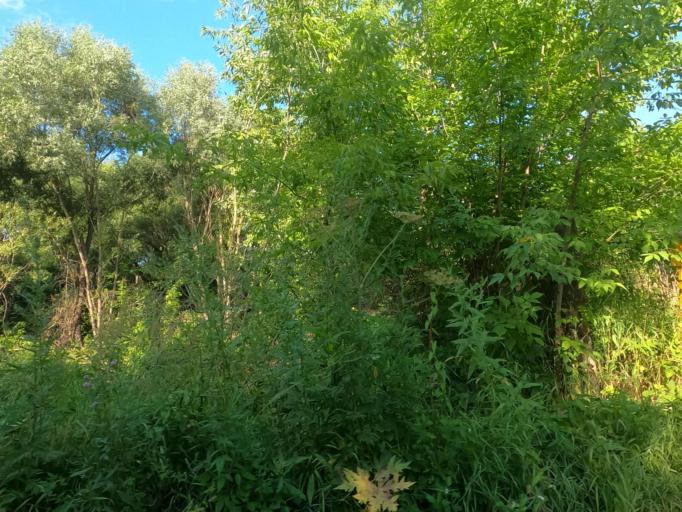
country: RU
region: Moskovskaya
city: Konobeyevo
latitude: 55.4129
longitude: 38.6950
